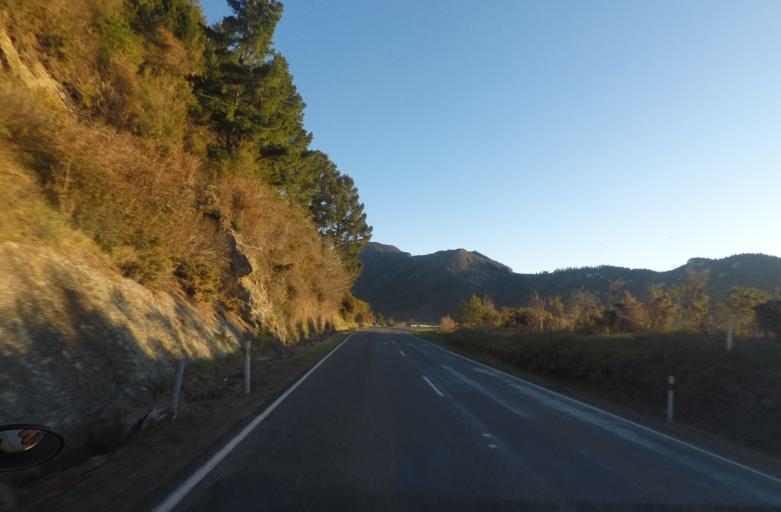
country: NZ
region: Marlborough
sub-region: Marlborough District
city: Picton
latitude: -41.2903
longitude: 173.6767
